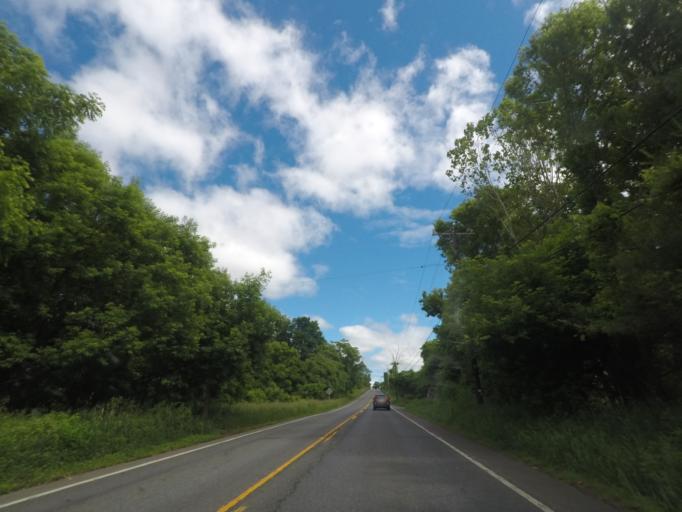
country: US
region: New York
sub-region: Columbia County
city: Philmont
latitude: 42.2188
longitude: -73.7097
